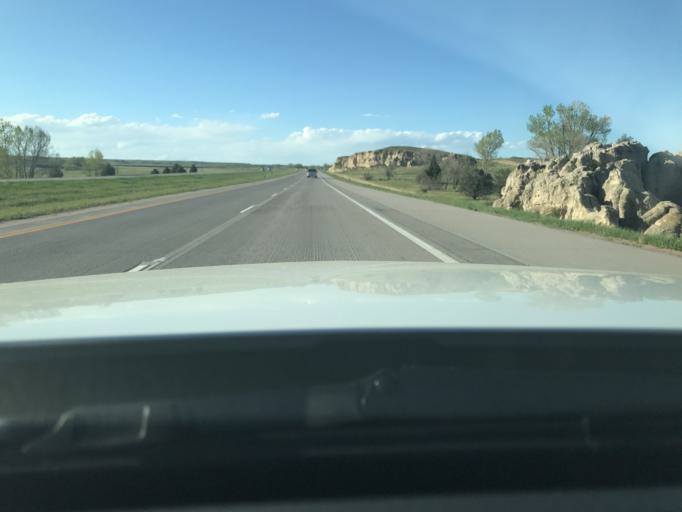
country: US
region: Wyoming
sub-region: Laramie County
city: South Greeley
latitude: 40.9528
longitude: -104.9239
